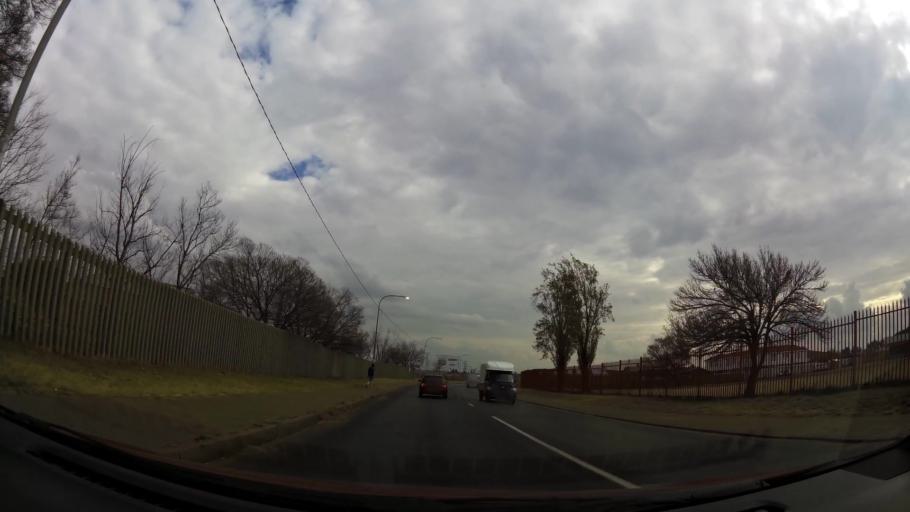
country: ZA
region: Gauteng
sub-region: City of Johannesburg Metropolitan Municipality
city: Soweto
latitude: -26.2396
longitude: 27.8540
